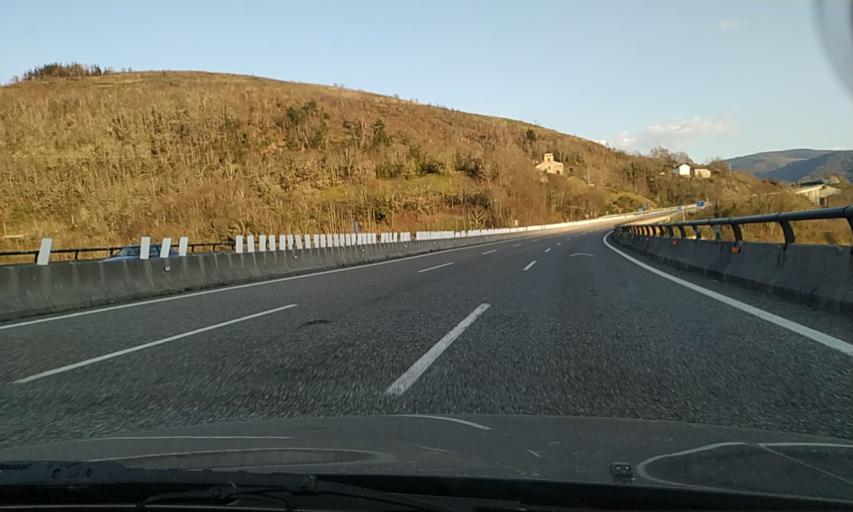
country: ES
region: Galicia
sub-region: Provincia de Lugo
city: San Roman
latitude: 42.7626
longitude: -7.0796
